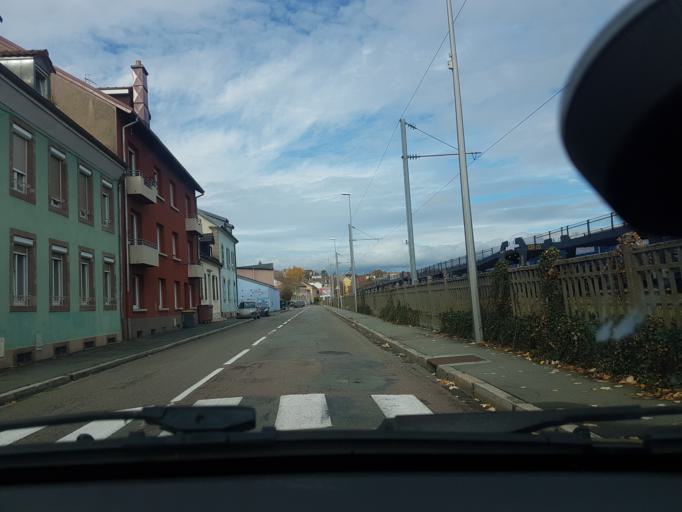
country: FR
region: Franche-Comte
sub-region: Territoire de Belfort
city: Belfort
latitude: 47.6306
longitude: 6.8531
